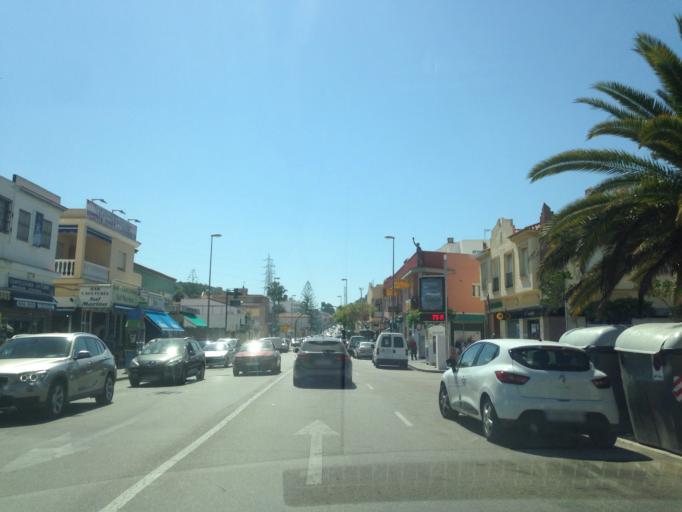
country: ES
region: Andalusia
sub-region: Provincia de Malaga
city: Malaga
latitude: 36.7381
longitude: -4.4807
